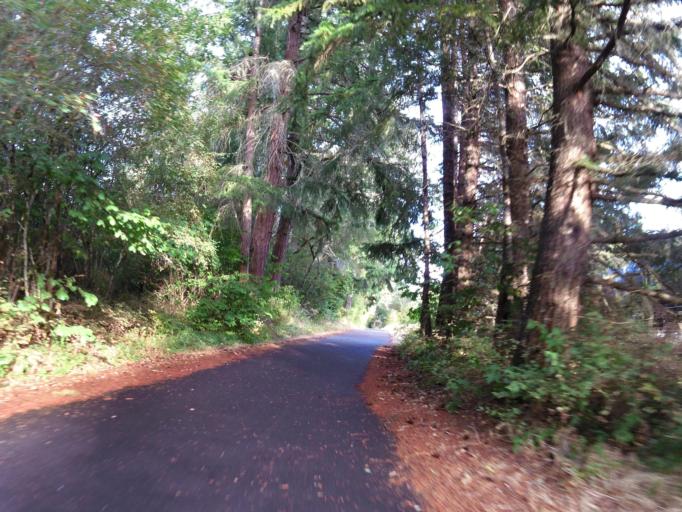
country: US
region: Washington
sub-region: Thurston County
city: Tenino
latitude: 46.9078
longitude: -122.7780
